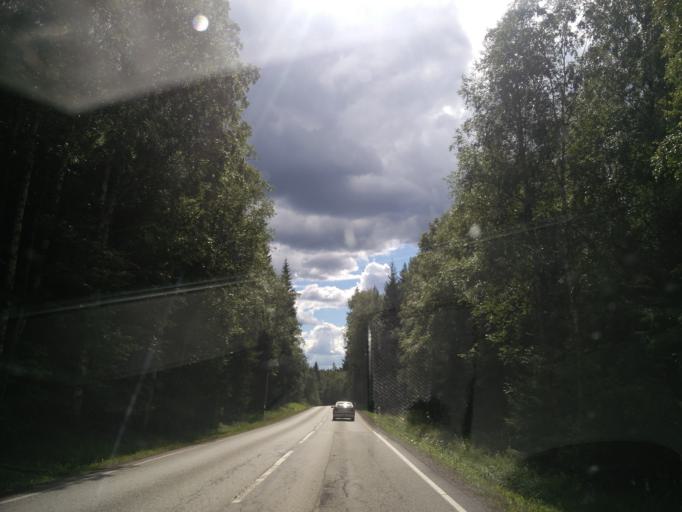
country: SE
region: OErebro
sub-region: Ljusnarsbergs Kommun
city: Kopparberg
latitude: 59.8434
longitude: 14.9987
